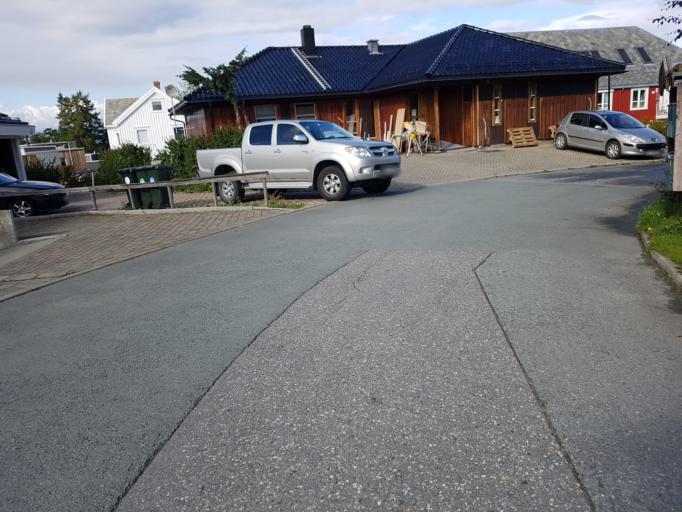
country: NO
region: Sor-Trondelag
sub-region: Trondheim
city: Trondheim
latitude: 63.4346
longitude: 10.4504
